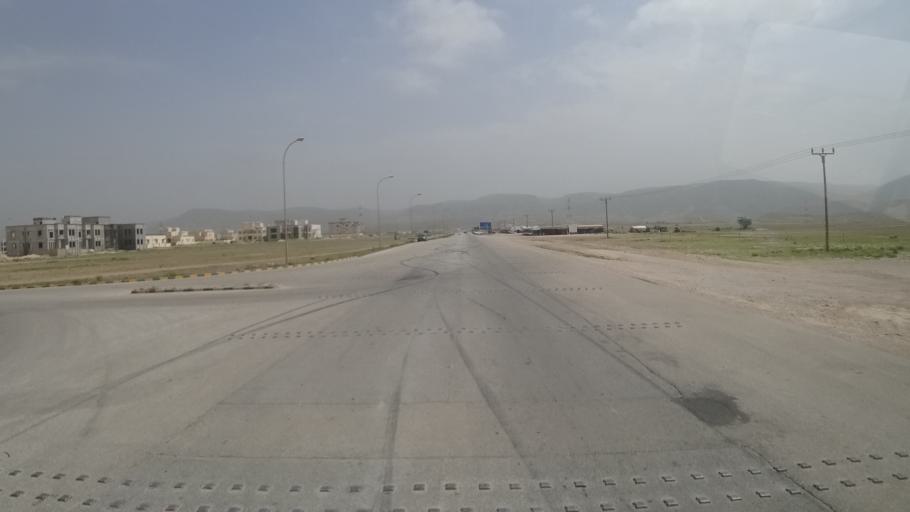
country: OM
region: Zufar
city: Salalah
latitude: 17.0973
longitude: 54.2168
